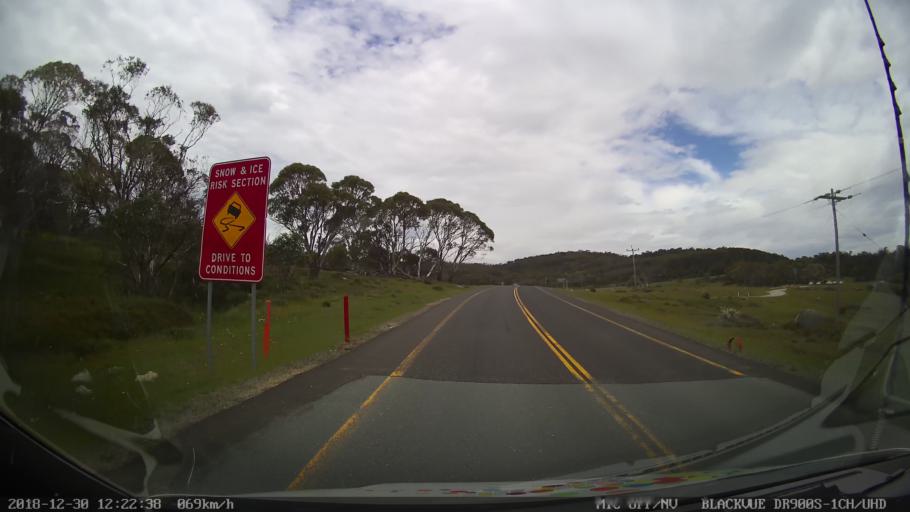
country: AU
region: New South Wales
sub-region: Snowy River
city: Jindabyne
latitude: -36.3605
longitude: 148.5087
